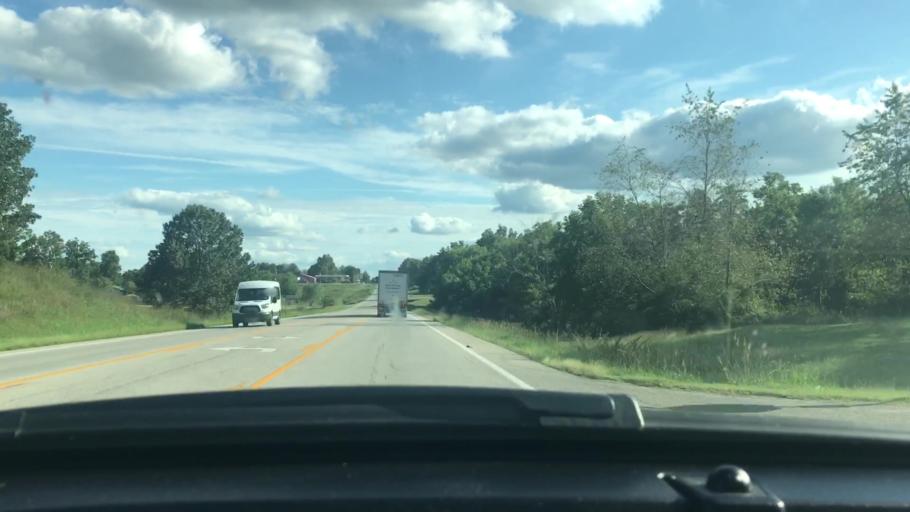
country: US
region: Missouri
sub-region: Oregon County
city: Thayer
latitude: 36.6002
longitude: -91.6440
